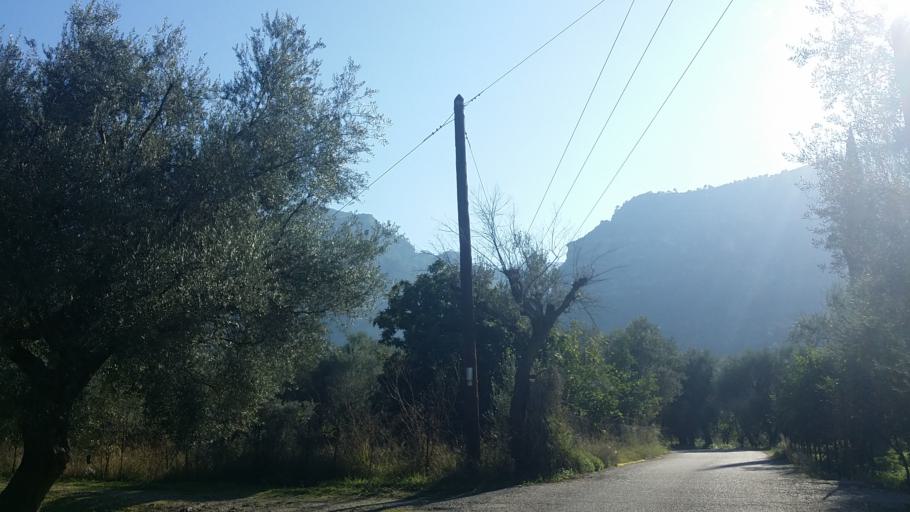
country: GR
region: West Greece
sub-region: Nomos Achaias
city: Temeni
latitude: 38.1908
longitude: 22.1879
